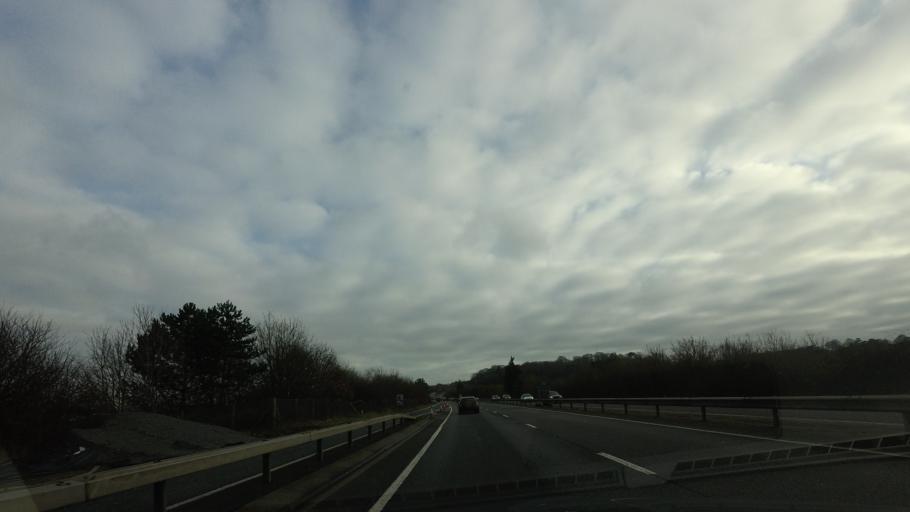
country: GB
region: England
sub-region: Kent
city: Tonbridge
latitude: 51.1837
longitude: 0.2487
